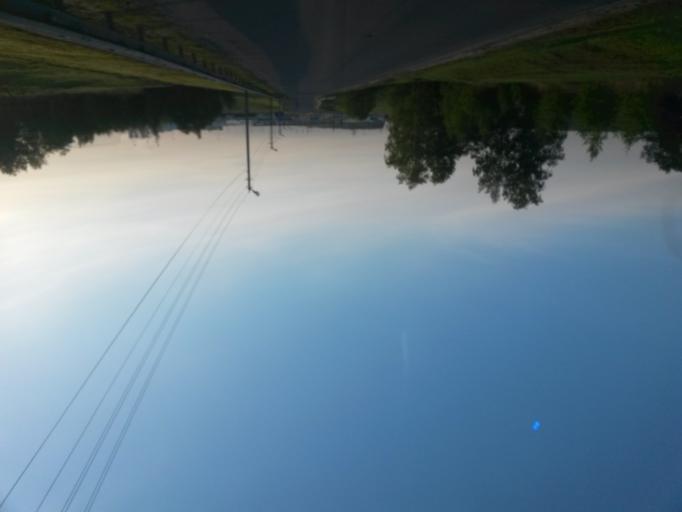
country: RU
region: Moskovskaya
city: Lyubuchany
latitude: 55.2487
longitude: 37.5330
